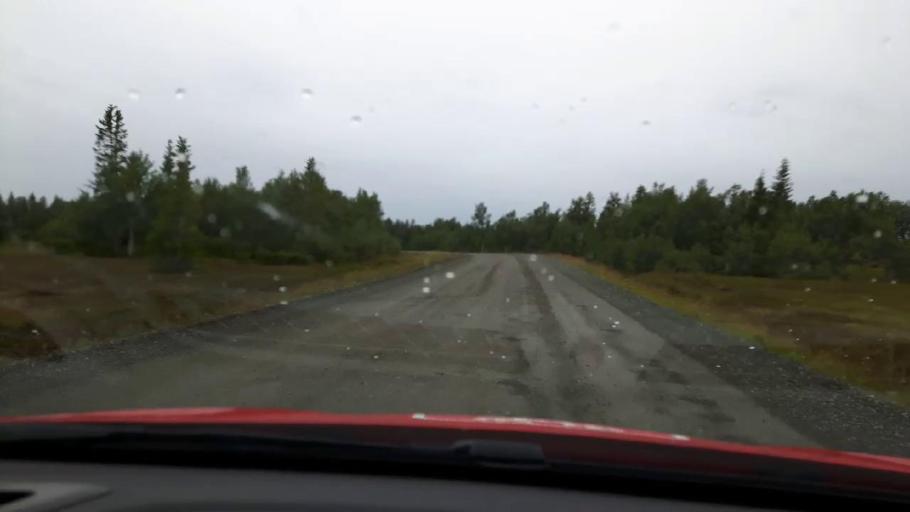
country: NO
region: Nord-Trondelag
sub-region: Meraker
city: Meraker
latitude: 63.5834
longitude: 12.2675
